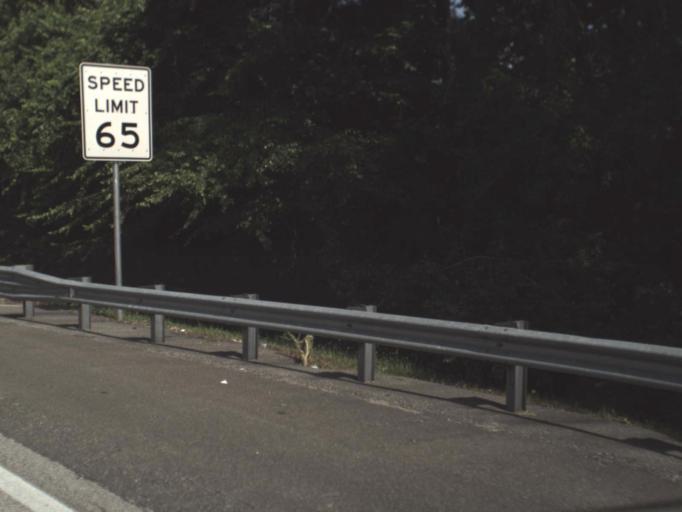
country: US
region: Florida
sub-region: Duval County
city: Jacksonville
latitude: 30.2501
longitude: -81.5633
